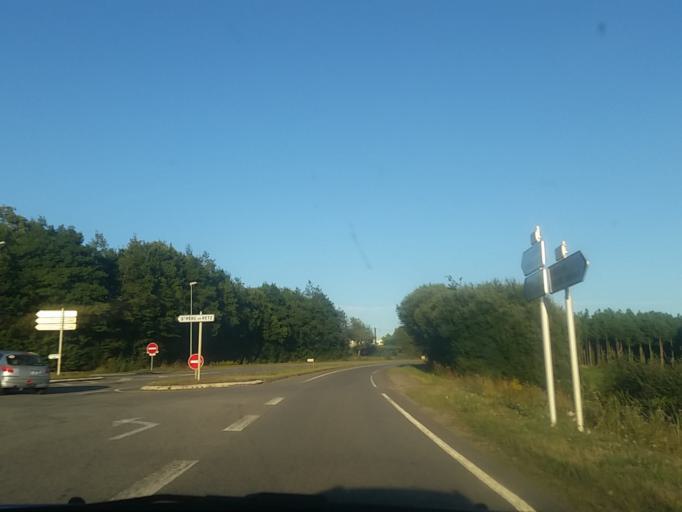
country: FR
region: Pays de la Loire
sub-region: Departement de la Loire-Atlantique
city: Saint-Pere-en-Retz
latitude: 47.2008
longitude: -2.0380
